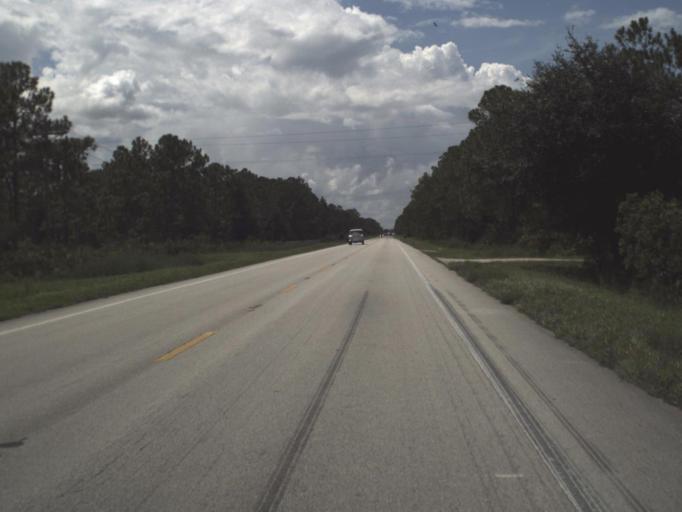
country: US
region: Florida
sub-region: Polk County
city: Babson Park
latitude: 27.8058
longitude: -81.2904
